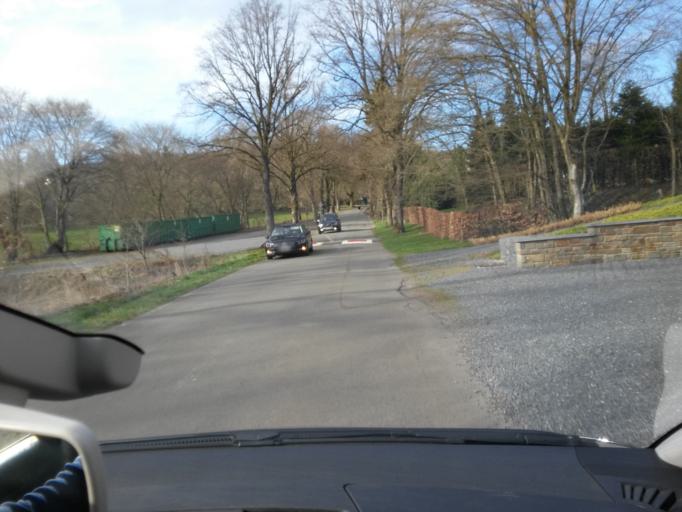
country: BE
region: Wallonia
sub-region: Province du Luxembourg
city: Daverdisse
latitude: 50.0042
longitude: 5.1578
